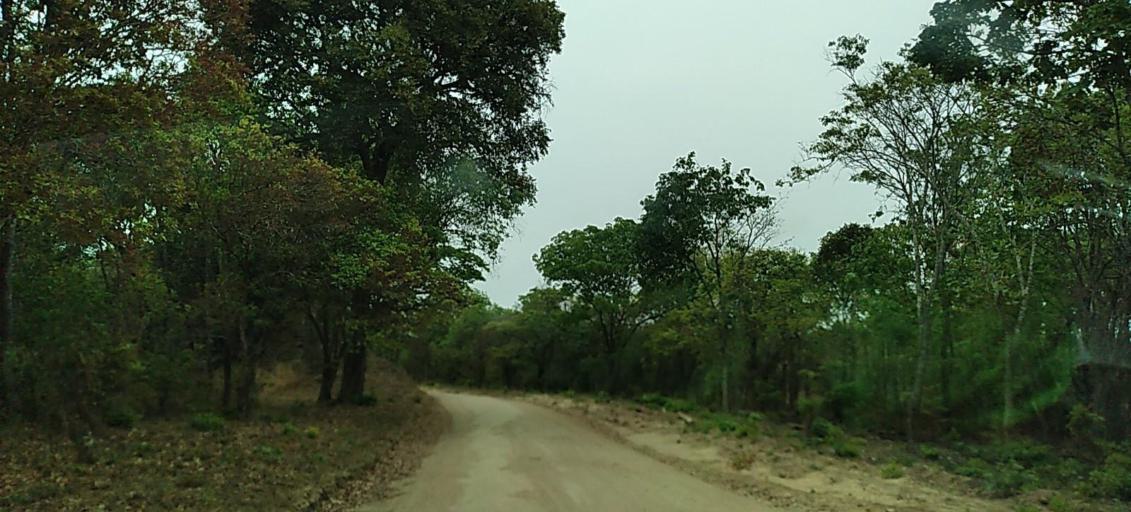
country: ZM
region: North-Western
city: Solwezi
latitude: -12.5368
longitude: 26.5234
